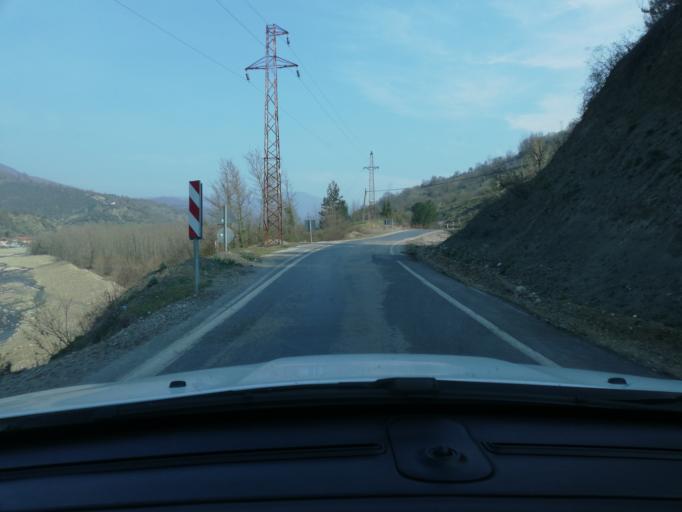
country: TR
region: Karabuk
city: Yenice
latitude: 41.2241
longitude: 32.3621
